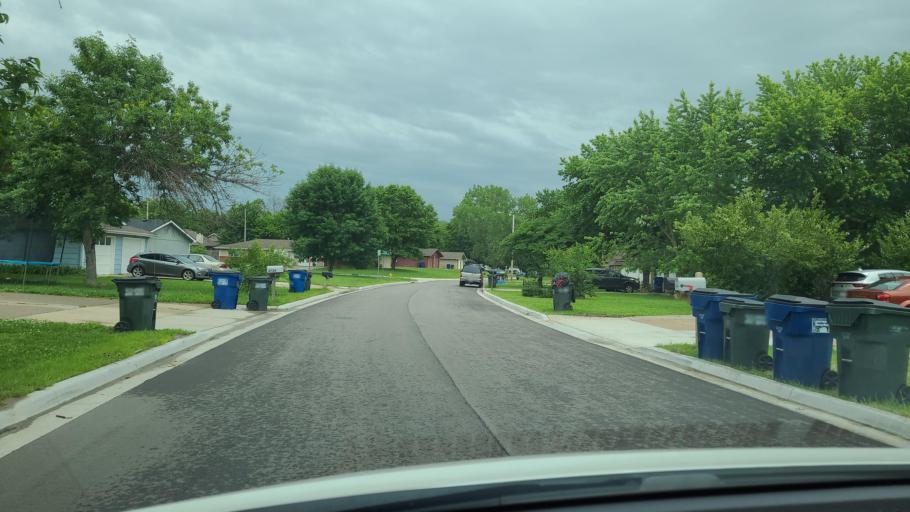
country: US
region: Kansas
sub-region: Douglas County
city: Lawrence
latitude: 38.9386
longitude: -95.2870
